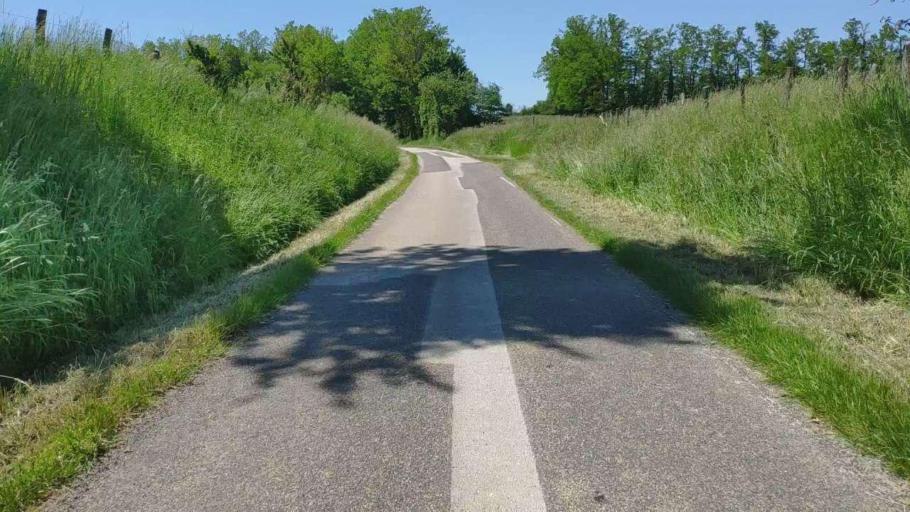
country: FR
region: Franche-Comte
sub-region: Departement du Jura
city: Bletterans
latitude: 46.7472
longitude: 5.3990
